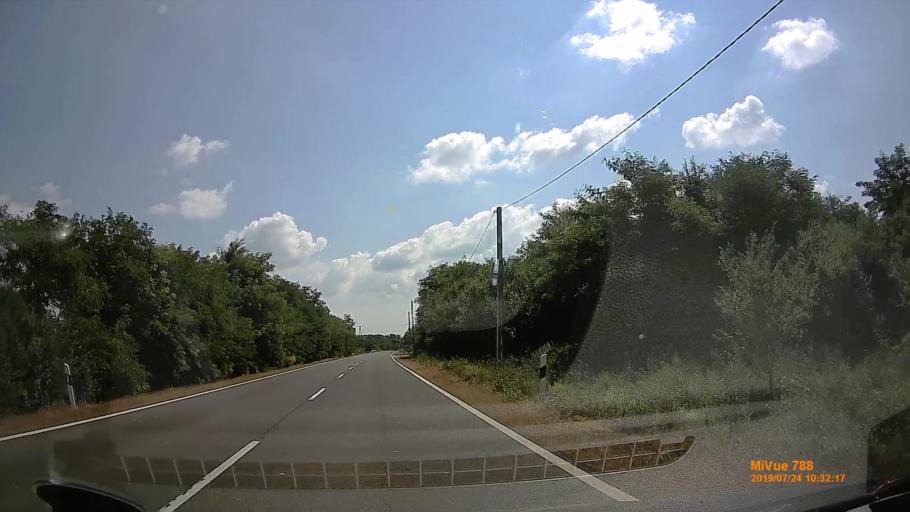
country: HU
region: Szabolcs-Szatmar-Bereg
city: Tarpa
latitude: 48.1600
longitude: 22.5322
